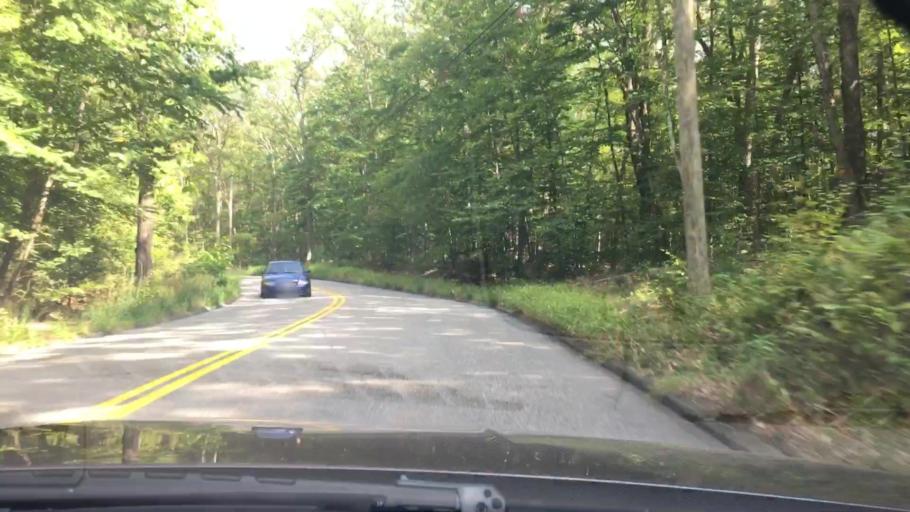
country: US
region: Connecticut
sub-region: Hartford County
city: Manchester
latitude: 41.7227
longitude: -72.5354
